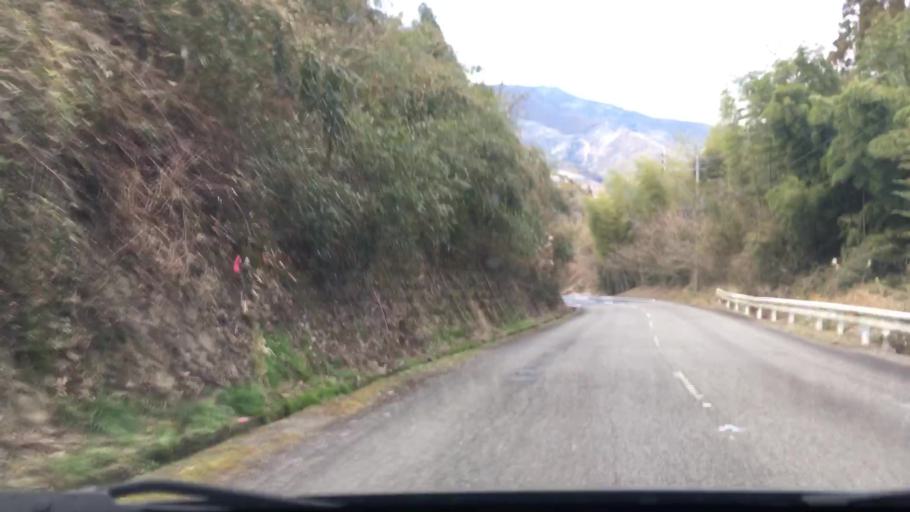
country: JP
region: Miyazaki
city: Nichinan
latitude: 31.7050
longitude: 131.3306
